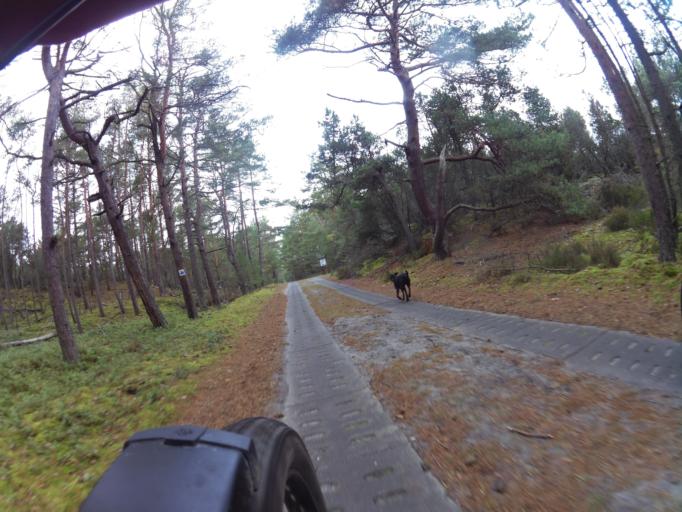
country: PL
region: Pomeranian Voivodeship
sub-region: Powiat pucki
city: Hel
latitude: 54.6226
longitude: 18.8190
